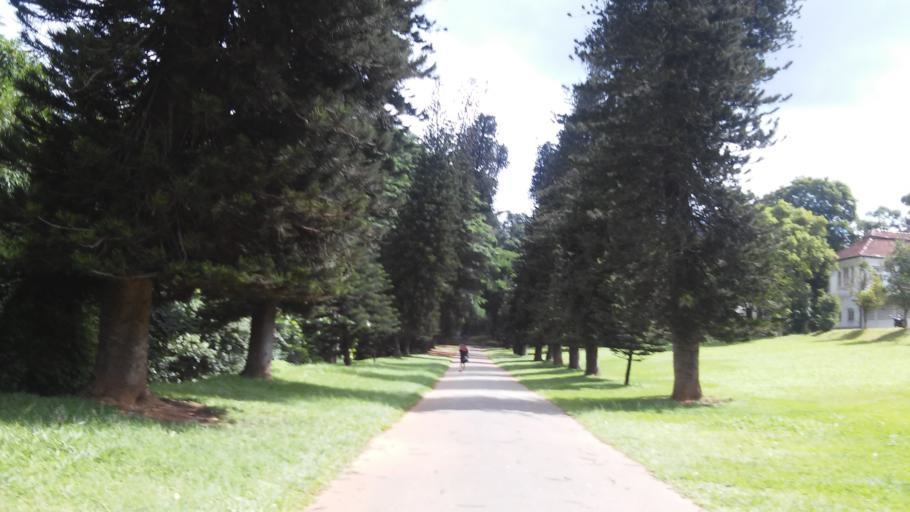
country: LK
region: Central
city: Kandy
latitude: 7.2702
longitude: 80.5939
